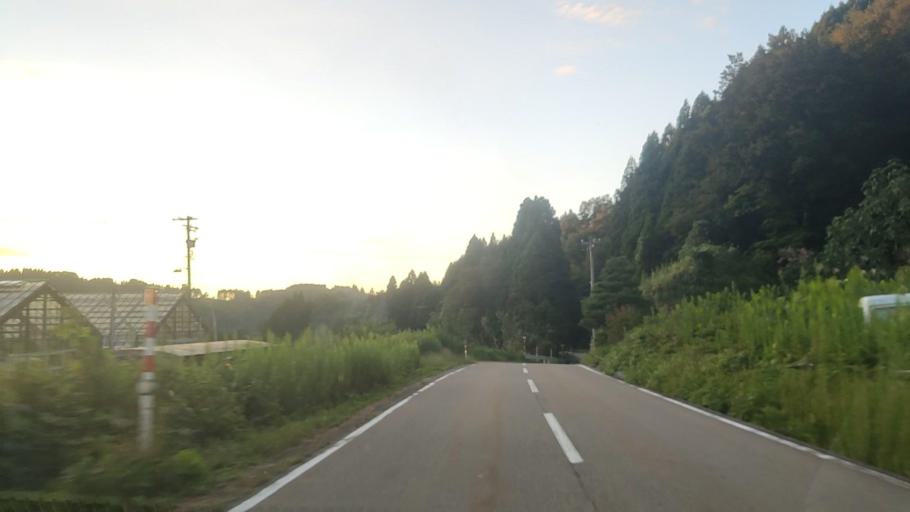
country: JP
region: Ishikawa
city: Tsubata
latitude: 36.6261
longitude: 136.7783
